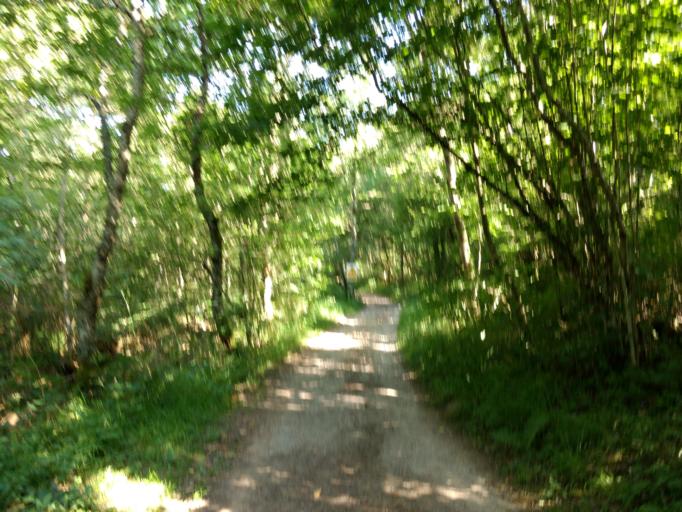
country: FR
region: Midi-Pyrenees
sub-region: Departement de l'Aveyron
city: La Loubiere
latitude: 44.3602
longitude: 2.6944
